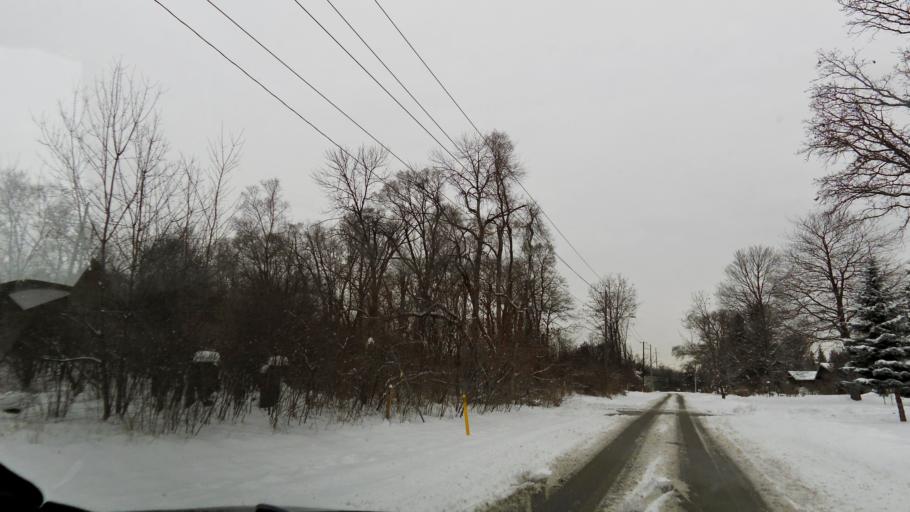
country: CA
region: Ontario
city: Mississauga
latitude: 43.5529
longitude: -79.6113
